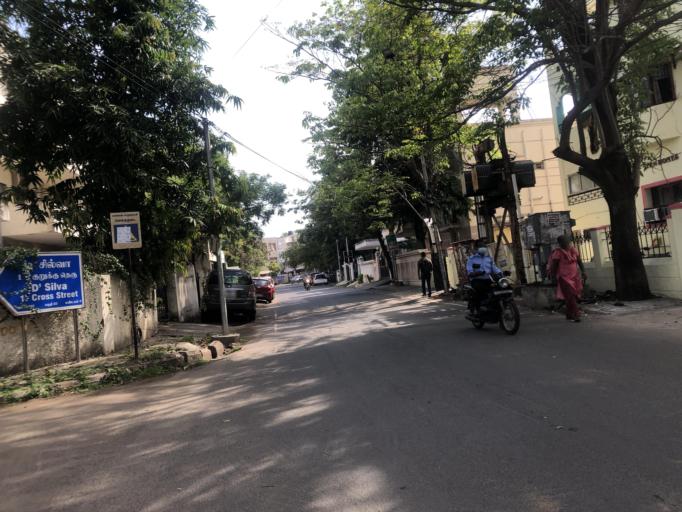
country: IN
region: Tamil Nadu
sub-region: Chennai
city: Gandhi Nagar
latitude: 13.0368
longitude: 80.2602
